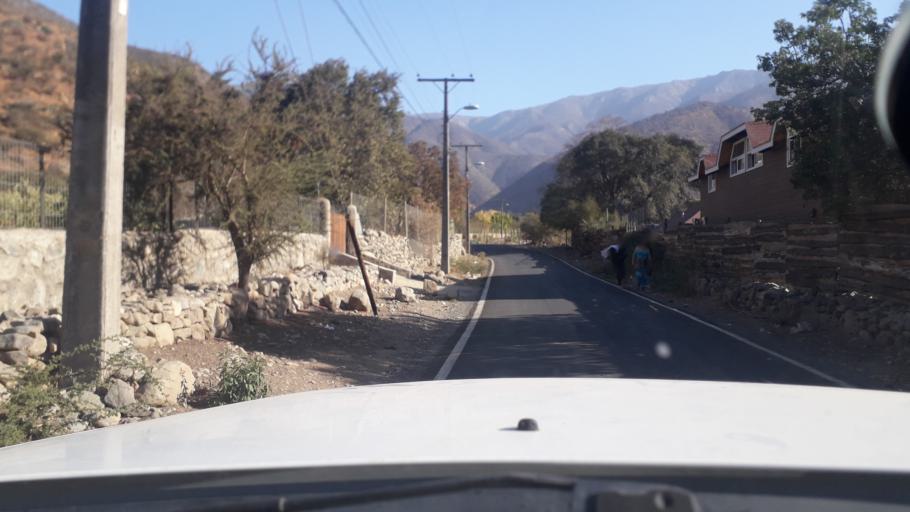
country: CL
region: Valparaiso
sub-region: Provincia de Marga Marga
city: Limache
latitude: -33.0587
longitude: -71.1151
